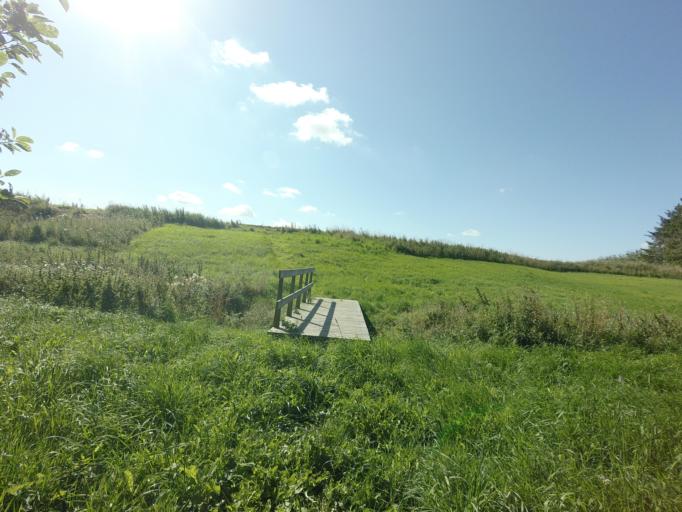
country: DK
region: North Denmark
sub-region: Hjorring Kommune
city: Vra
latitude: 57.3993
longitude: 9.7985
